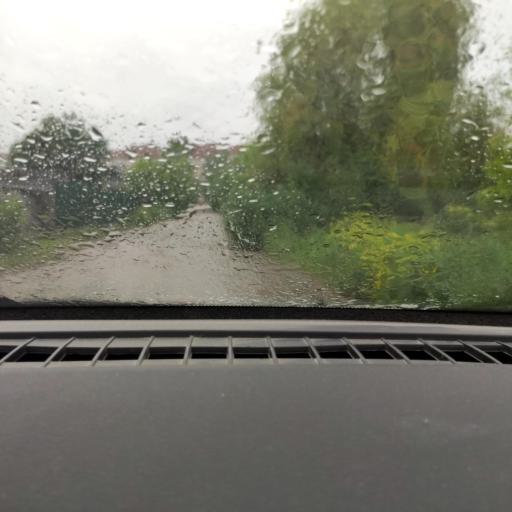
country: RU
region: Perm
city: Perm
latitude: 58.0337
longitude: 56.3611
